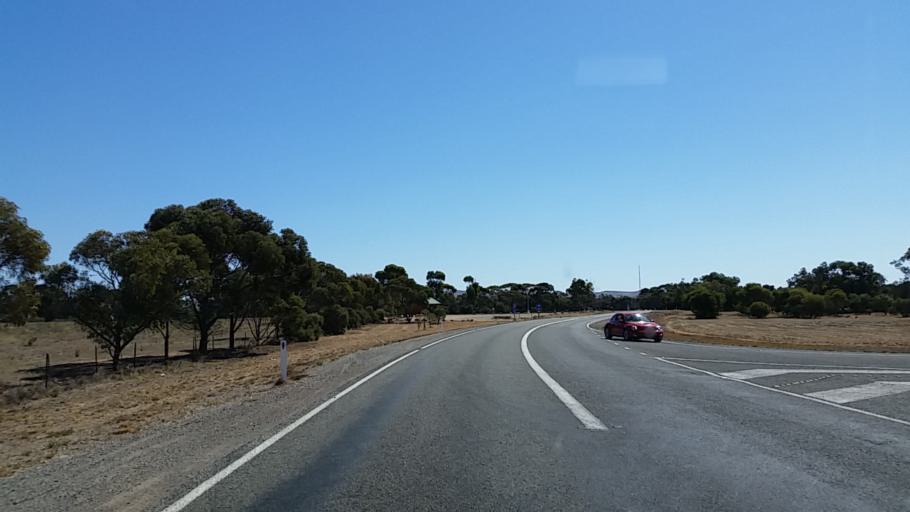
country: AU
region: South Australia
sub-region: Peterborough
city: Peterborough
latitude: -32.7393
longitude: 138.6217
